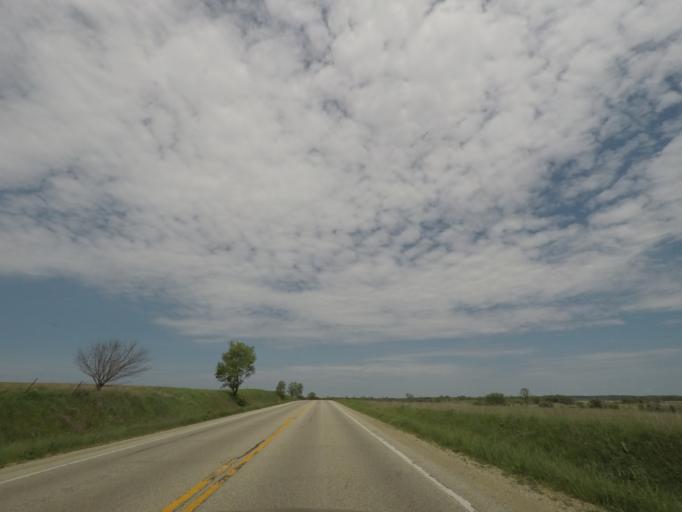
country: US
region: Wisconsin
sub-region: Rock County
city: Evansville
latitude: 42.7542
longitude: -89.2990
